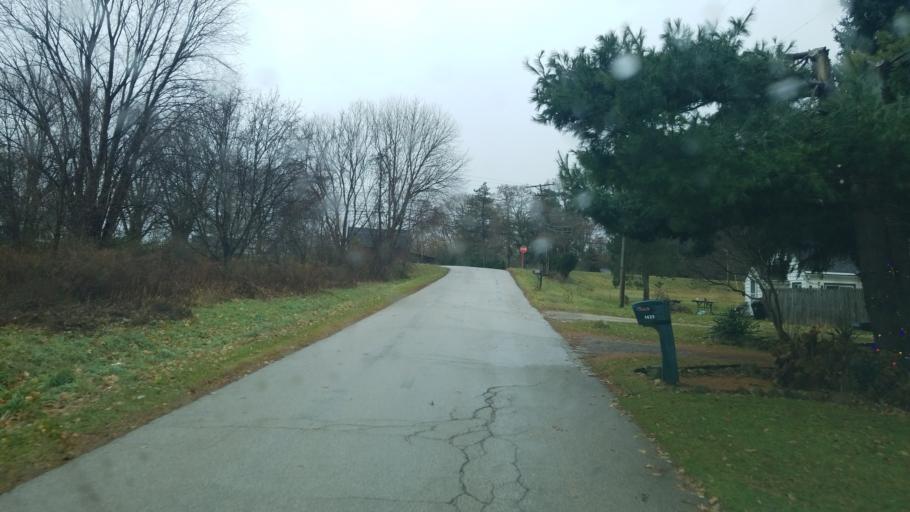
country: US
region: Ohio
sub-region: Ashtabula County
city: North Kingsville
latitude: 41.8938
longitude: -80.7232
